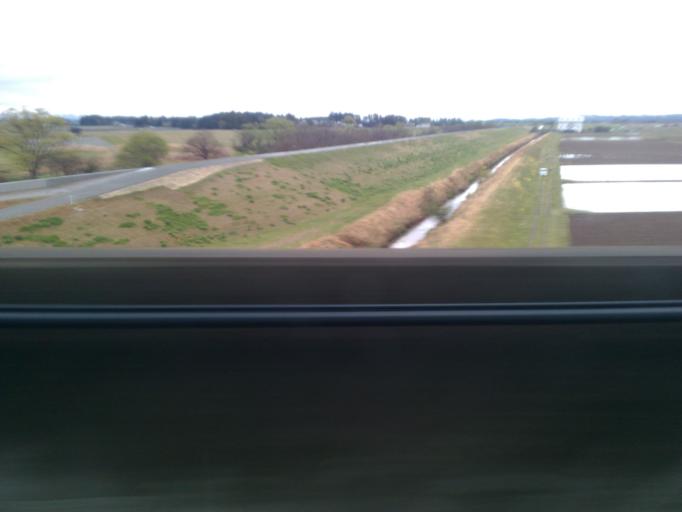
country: JP
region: Miyagi
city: Furukawa
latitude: 38.5414
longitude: 140.9612
